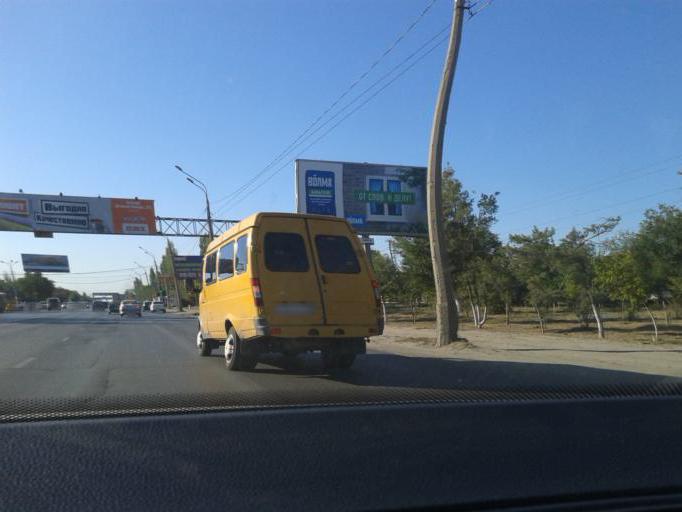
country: RU
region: Volgograd
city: Gorodishche
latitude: 48.7626
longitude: 44.4764
